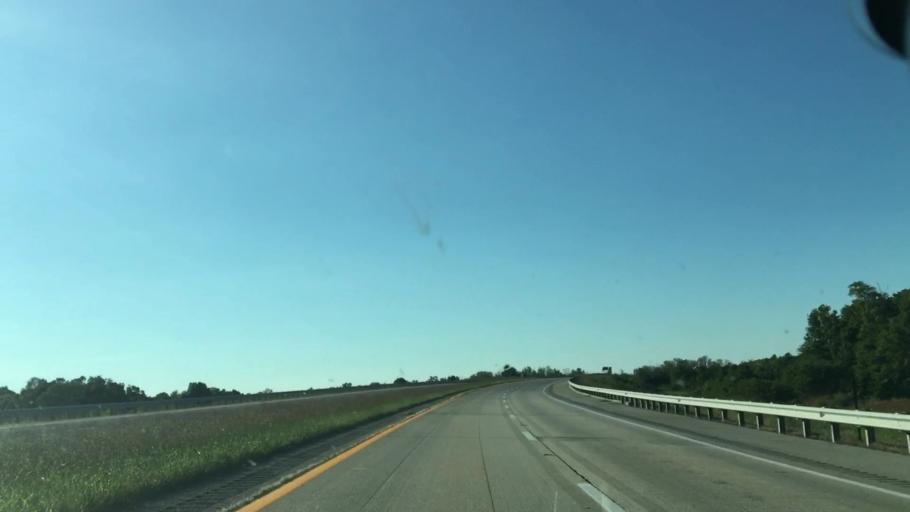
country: US
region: Kentucky
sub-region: Daviess County
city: Owensboro
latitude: 37.7531
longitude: -87.2928
